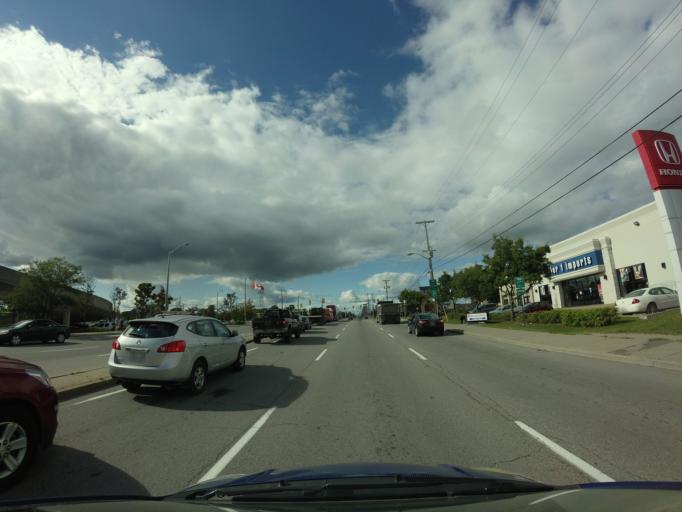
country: CA
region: Ontario
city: Ottawa
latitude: 45.4234
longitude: -75.6368
